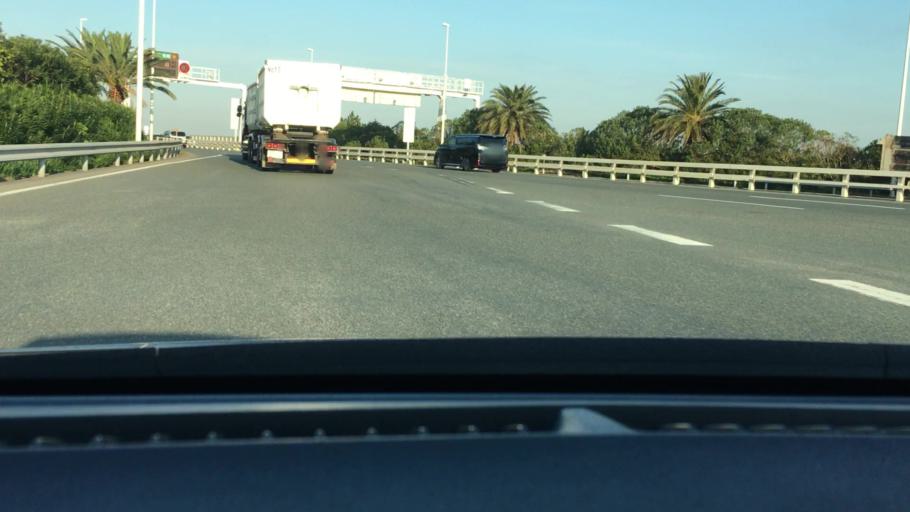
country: JP
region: Chiba
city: Kisarazu
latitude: 35.4361
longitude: 139.9174
